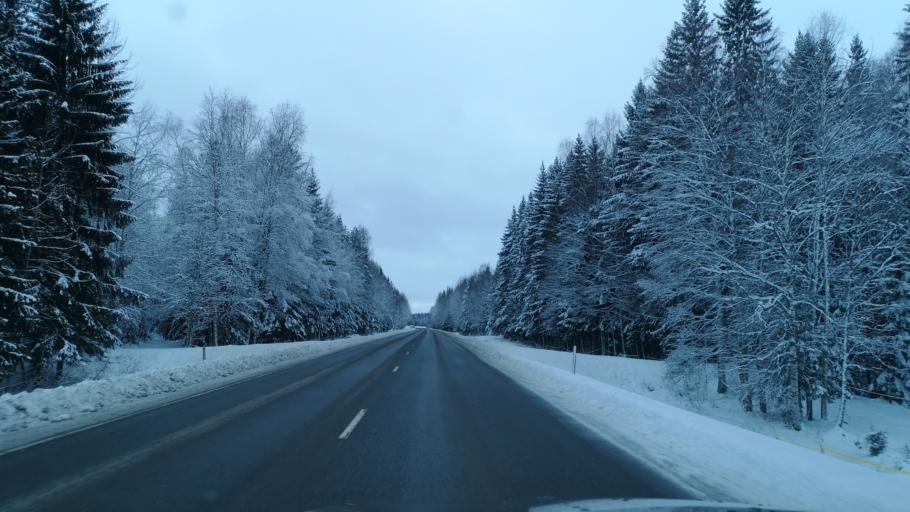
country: FI
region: Varsinais-Suomi
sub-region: Loimaa
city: Loimaa
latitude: 60.9118
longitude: 23.1739
